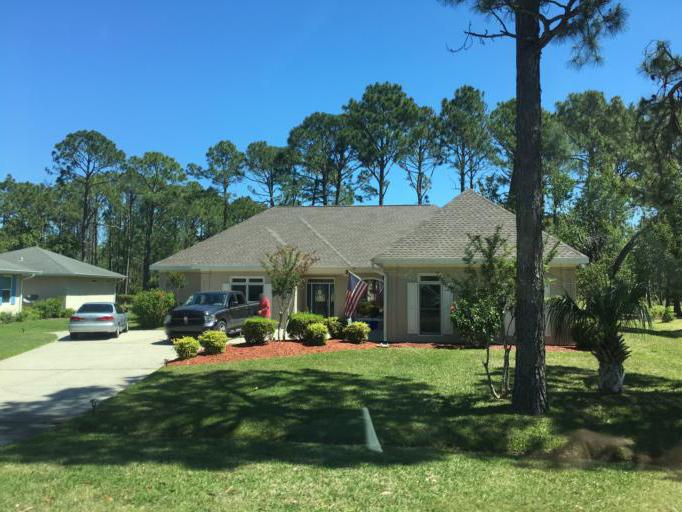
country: US
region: Florida
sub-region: Bay County
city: Panama City Beach
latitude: 30.1917
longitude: -85.8112
